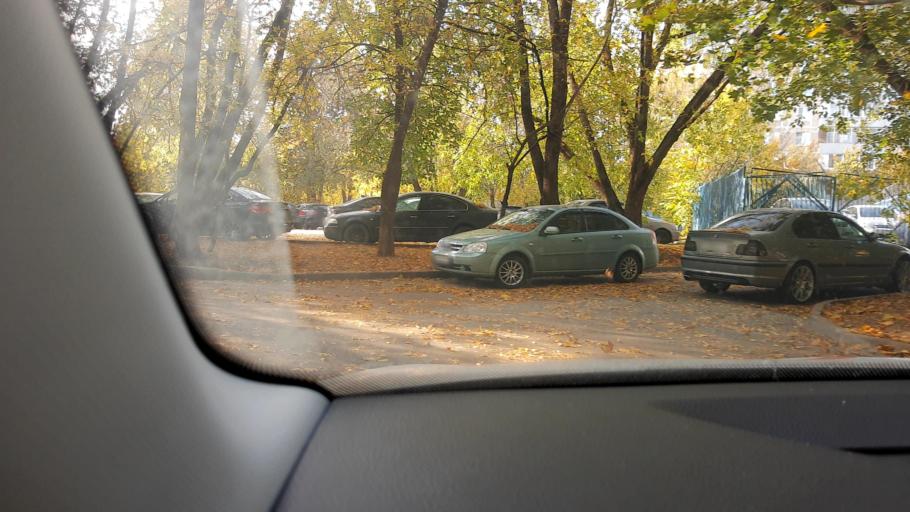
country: RU
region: Moscow
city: Nagornyy
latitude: 55.6245
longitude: 37.6036
